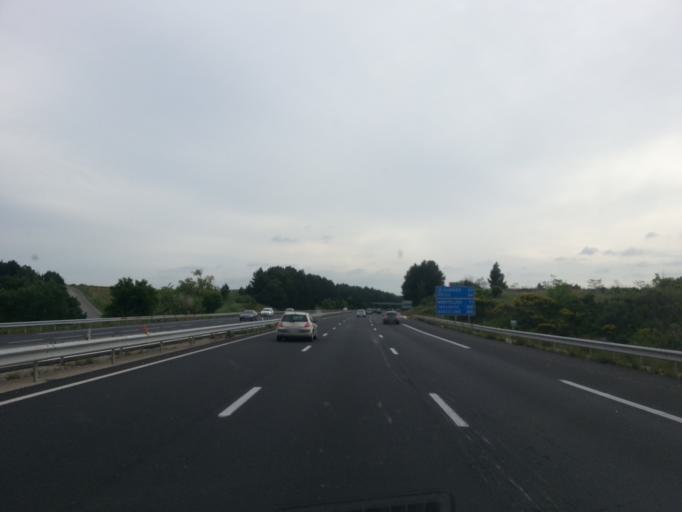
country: FR
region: Languedoc-Roussillon
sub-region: Departement du Gard
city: Remoulins
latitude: 43.9309
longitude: 4.5957
